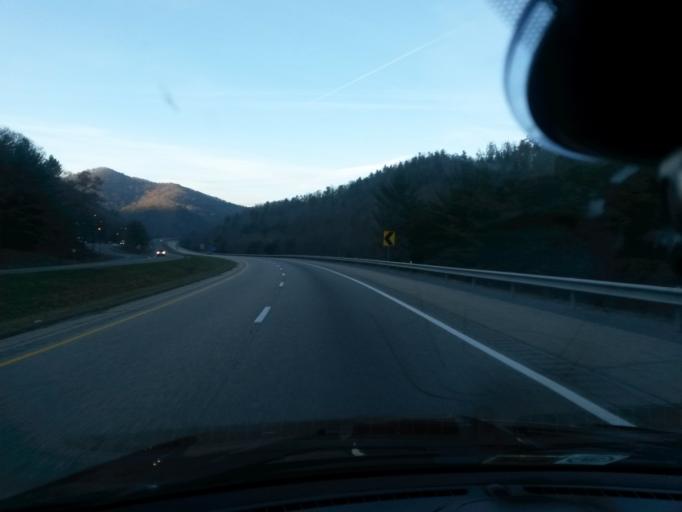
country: US
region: West Virginia
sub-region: Greenbrier County
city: White Sulphur Springs
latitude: 37.8136
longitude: -80.1868
